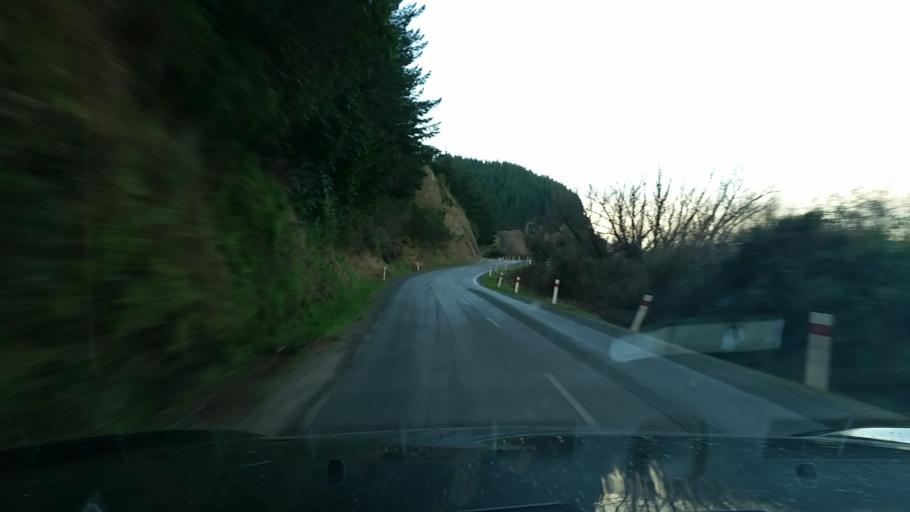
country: NZ
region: Marlborough
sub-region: Marlborough District
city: Blenheim
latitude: -41.5205
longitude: 173.6068
